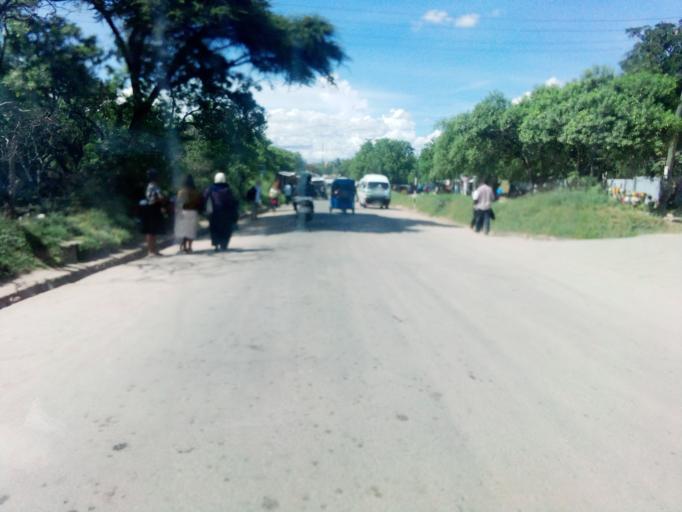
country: TZ
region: Dodoma
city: Dodoma
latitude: -6.1787
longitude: 35.7526
